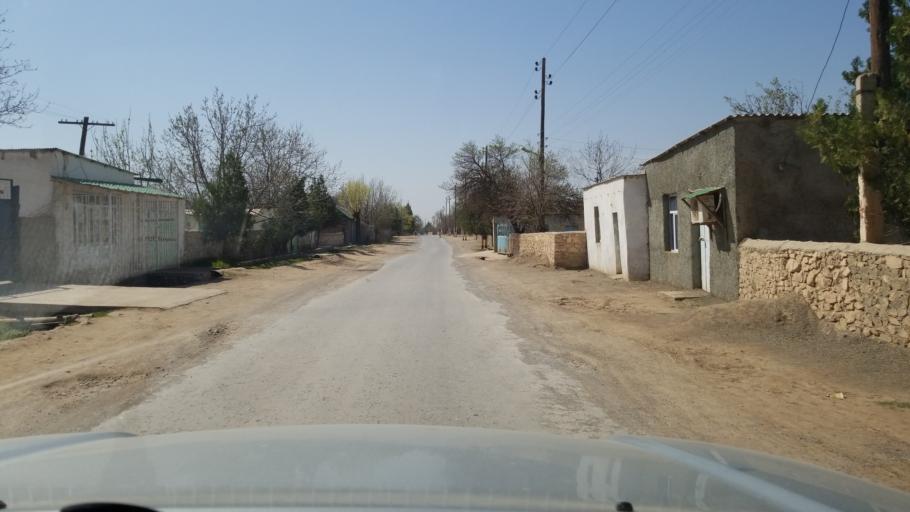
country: TM
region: Lebap
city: Gowurdak
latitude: 37.9100
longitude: 66.4748
